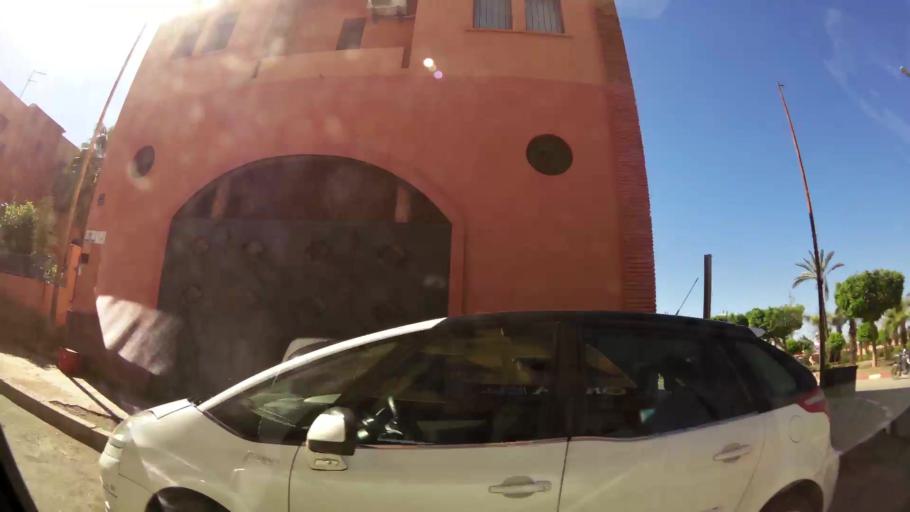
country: MA
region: Marrakech-Tensift-Al Haouz
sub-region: Marrakech
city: Marrakesh
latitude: 31.6455
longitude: -7.9853
